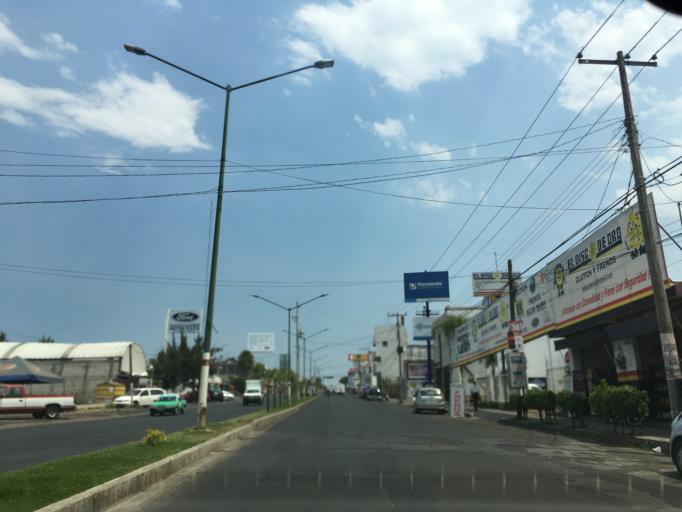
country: MX
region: Guanajuato
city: Moroleon
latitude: 20.1242
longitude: -101.1797
